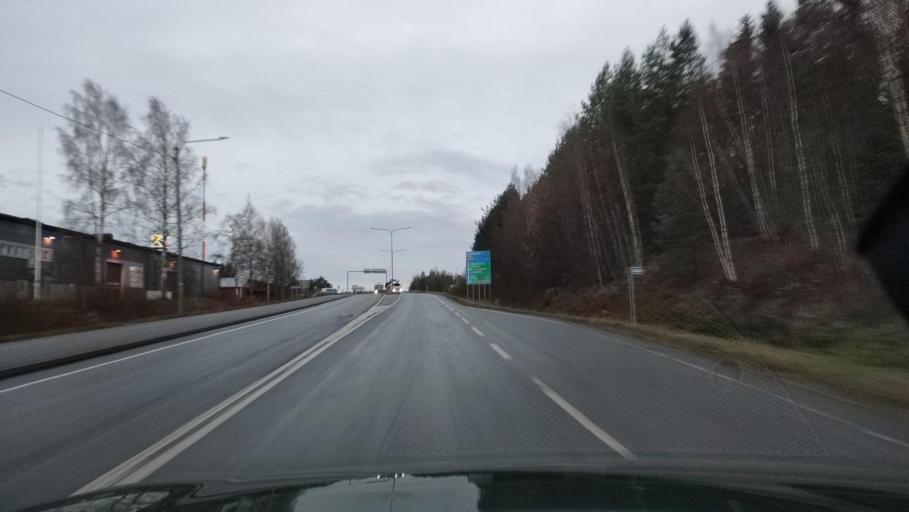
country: FI
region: Ostrobothnia
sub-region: Vaasa
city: Ristinummi
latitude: 63.0308
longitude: 21.7572
